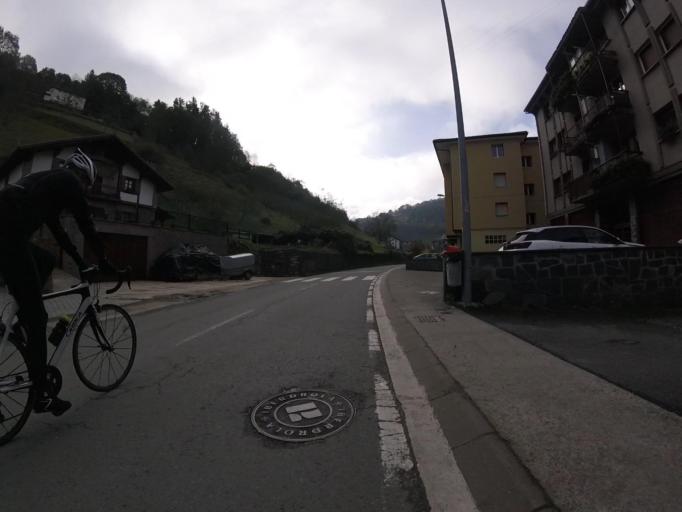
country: ES
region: Navarre
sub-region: Provincia de Navarra
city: Goizueta
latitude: 43.1742
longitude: -1.8630
